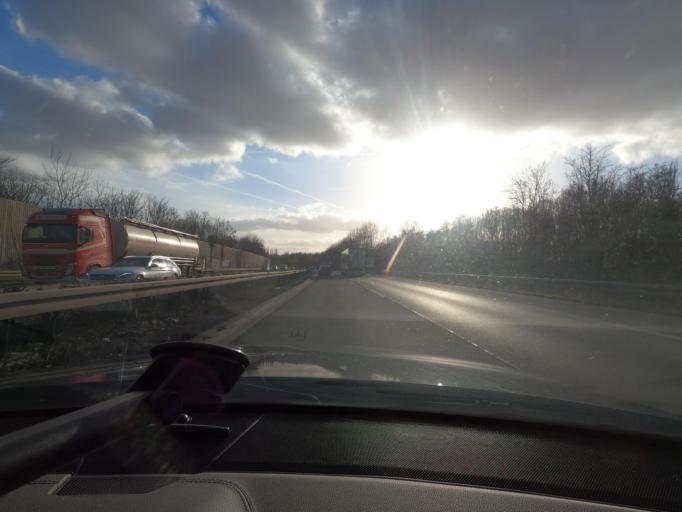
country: DE
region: North Rhine-Westphalia
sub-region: Regierungsbezirk Arnsberg
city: Dortmund
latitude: 51.5469
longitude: 7.5141
